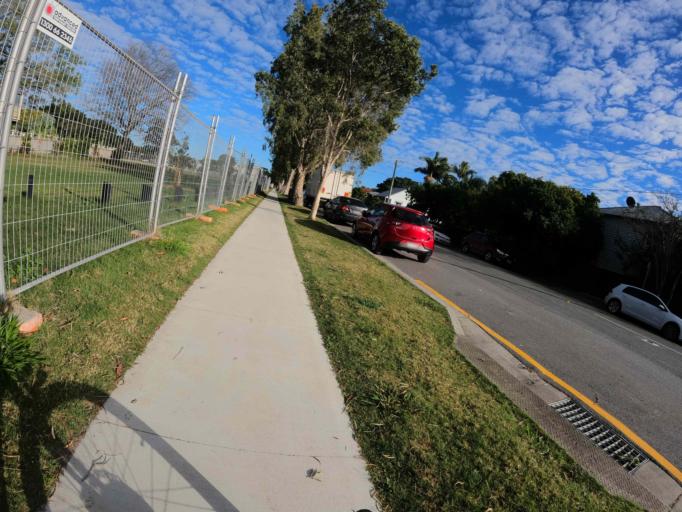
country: AU
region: Queensland
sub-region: Brisbane
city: Windsor
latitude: -27.4416
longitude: 153.0293
